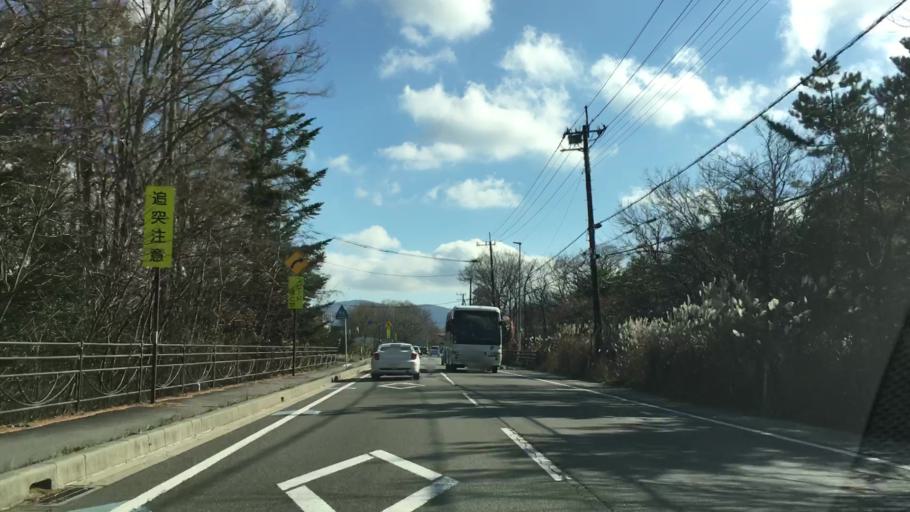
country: JP
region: Shizuoka
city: Gotemba
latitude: 35.4339
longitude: 138.8418
